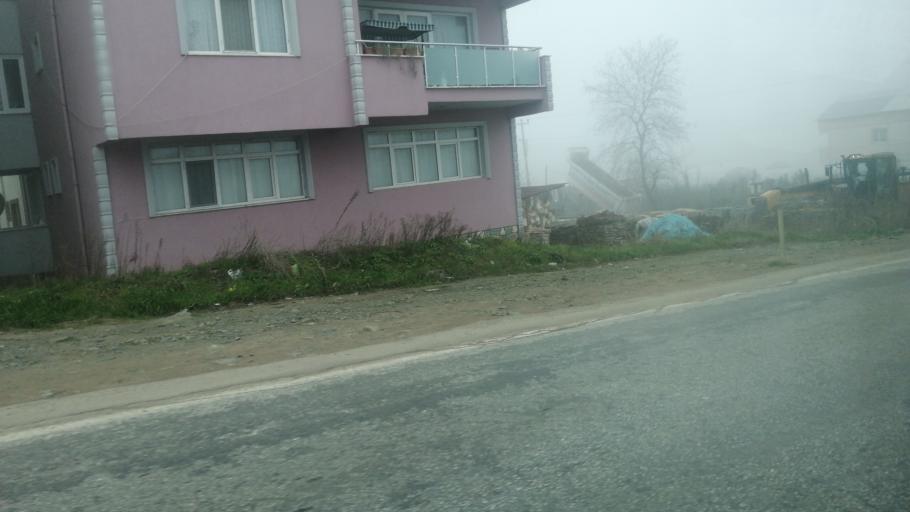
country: TR
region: Yalova
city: Korukoy
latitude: 40.6542
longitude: 29.1933
